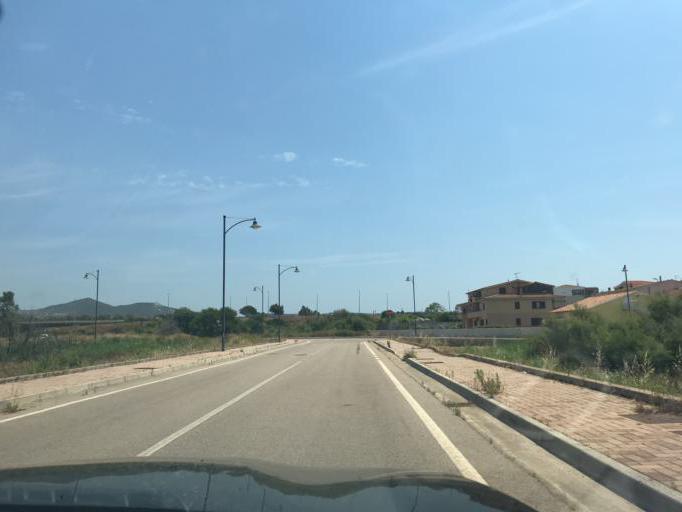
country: IT
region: Sardinia
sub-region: Provincia di Olbia-Tempio
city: Olbia
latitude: 40.9312
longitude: 9.5059
